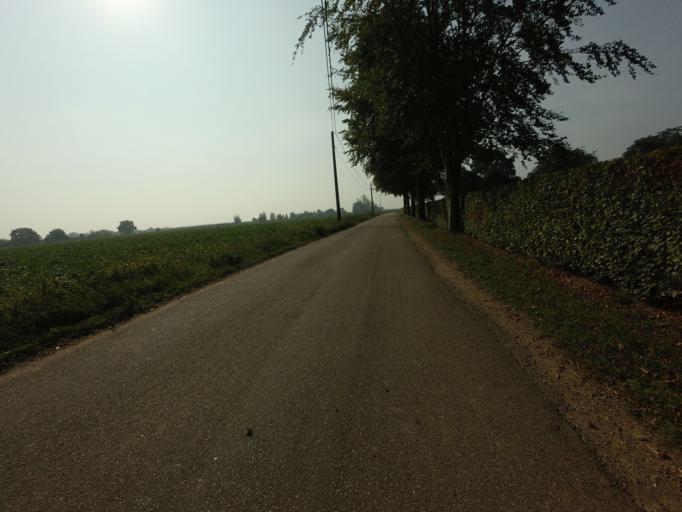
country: NL
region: Limburg
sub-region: Gemeente Maasgouw
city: Maasbracht
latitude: 51.1549
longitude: 5.8294
